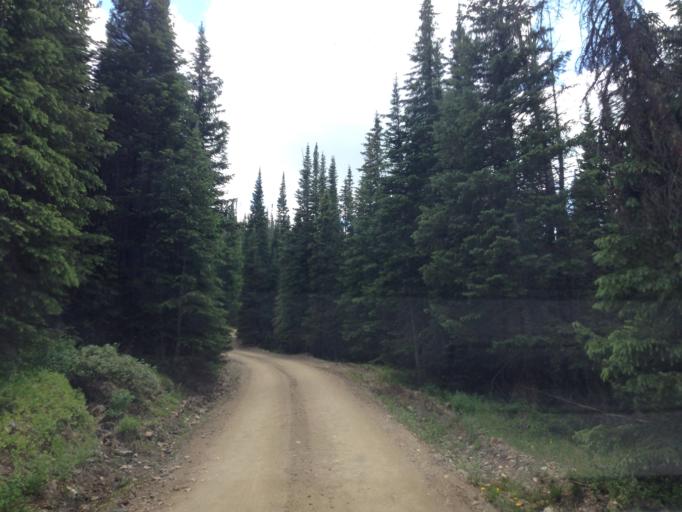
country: US
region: Colorado
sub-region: Larimer County
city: Estes Park
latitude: 40.5008
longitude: -105.8983
